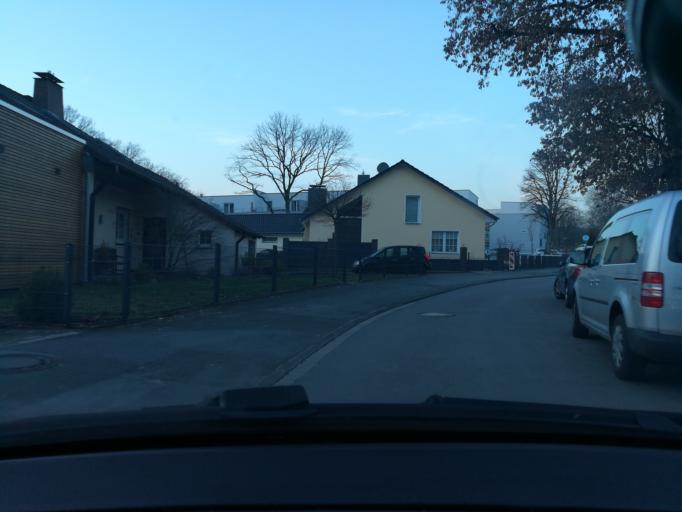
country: DE
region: North Rhine-Westphalia
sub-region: Regierungsbezirk Detmold
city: Oerlinghausen
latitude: 51.9515
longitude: 8.5921
